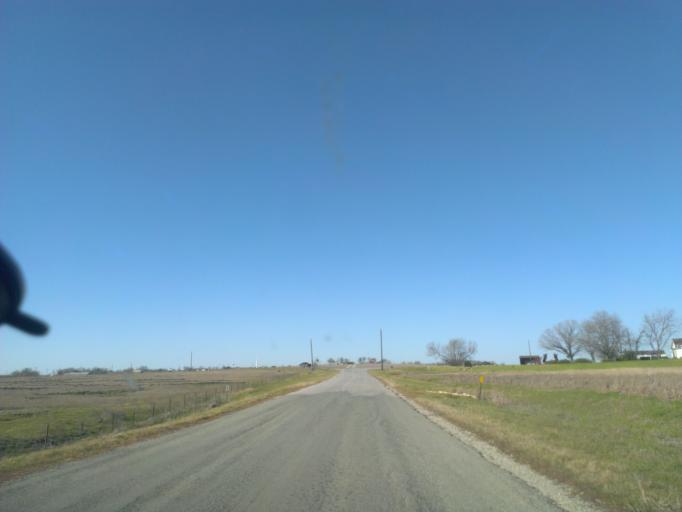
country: US
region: Texas
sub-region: Milam County
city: Thorndale
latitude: 30.5533
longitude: -97.2985
